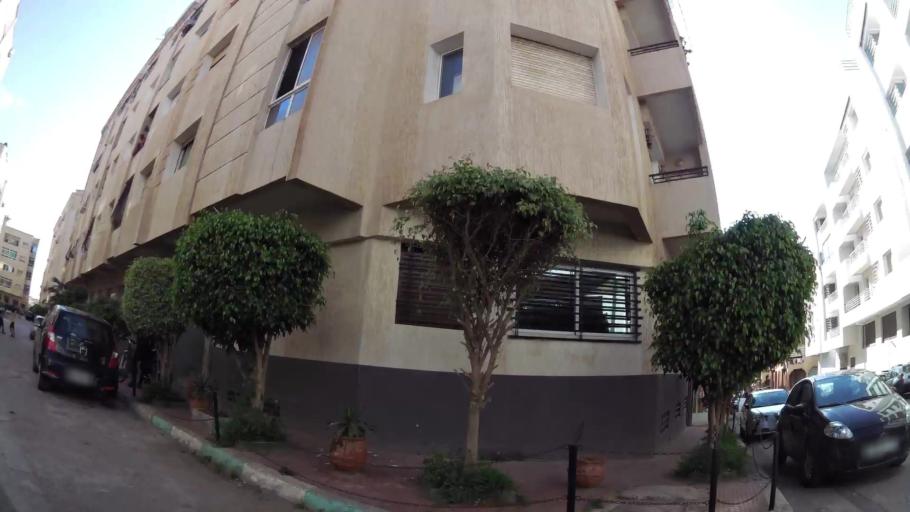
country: MA
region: Rabat-Sale-Zemmour-Zaer
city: Sale
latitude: 34.0497
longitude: -6.8001
